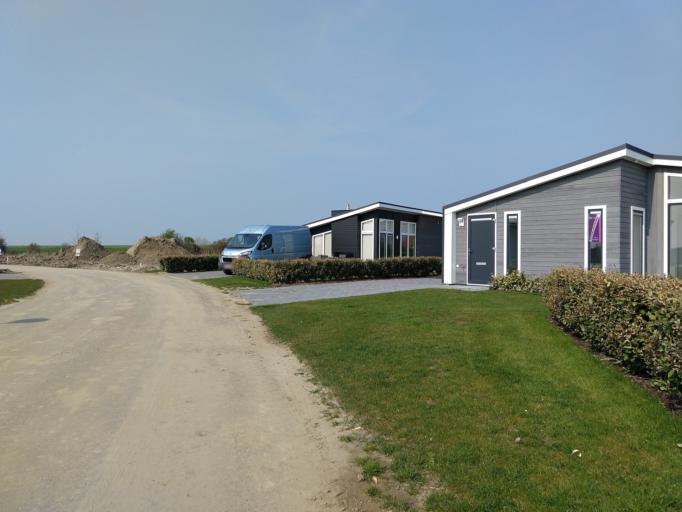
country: NL
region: Zeeland
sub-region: Gemeente Reimerswaal
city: Yerseke
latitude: 51.5230
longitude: 3.9804
